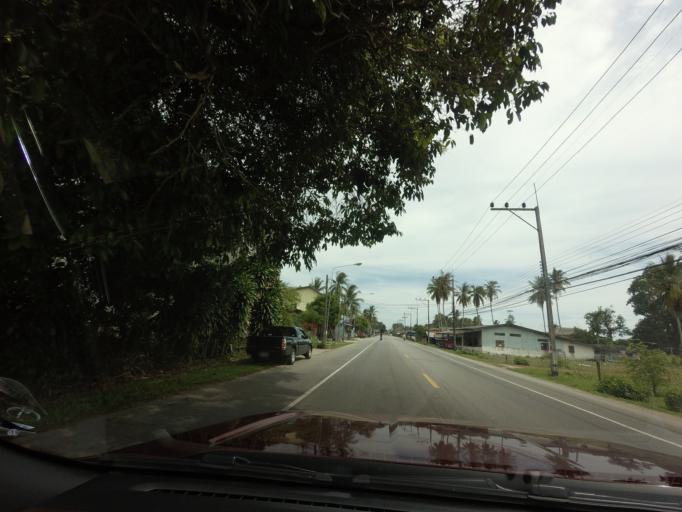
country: TH
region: Narathiwat
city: Tak Bai
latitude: 6.2466
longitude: 102.0717
